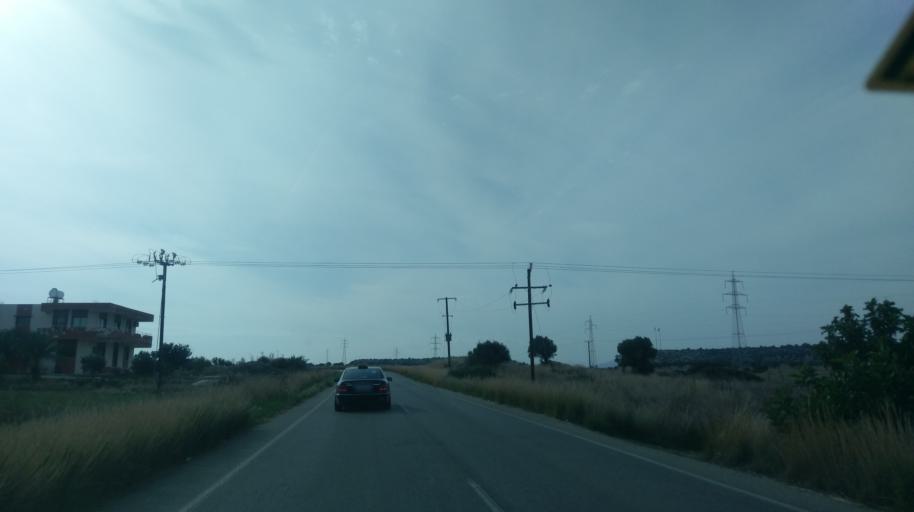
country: CY
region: Ammochostos
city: Leonarisso
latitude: 35.3952
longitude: 34.0628
